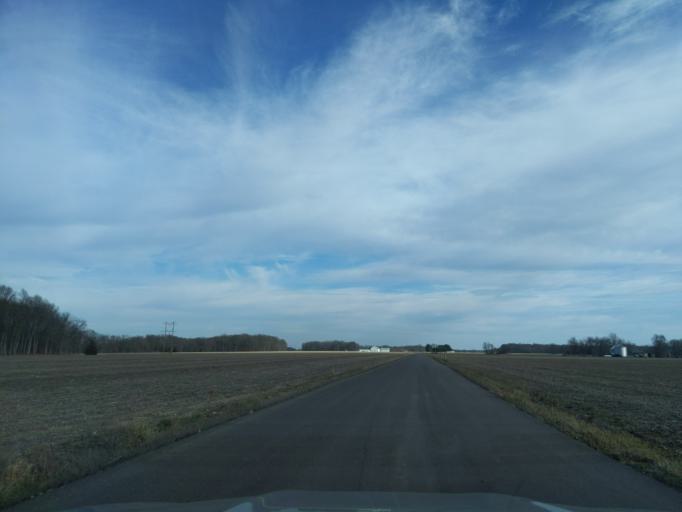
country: US
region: Indiana
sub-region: Decatur County
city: Greensburg
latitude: 39.2338
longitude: -85.4291
